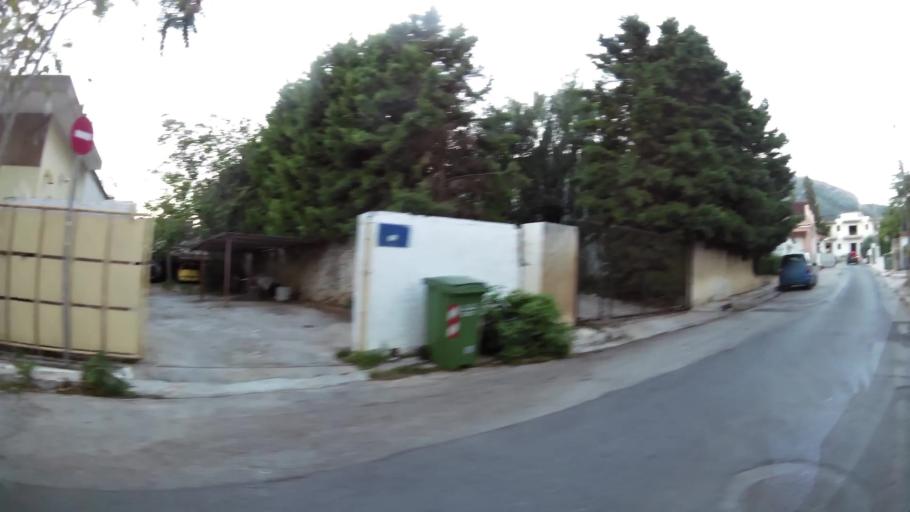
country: GR
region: Attica
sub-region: Nomarchia Anatolikis Attikis
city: Paiania
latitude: 37.9541
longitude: 23.8499
